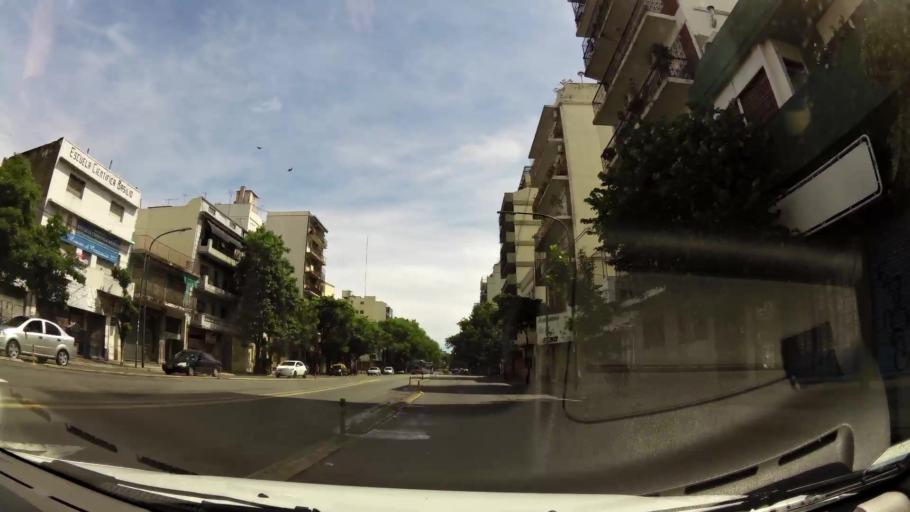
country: AR
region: Buenos Aires F.D.
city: Villa Santa Rita
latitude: -34.6060
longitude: -58.4608
